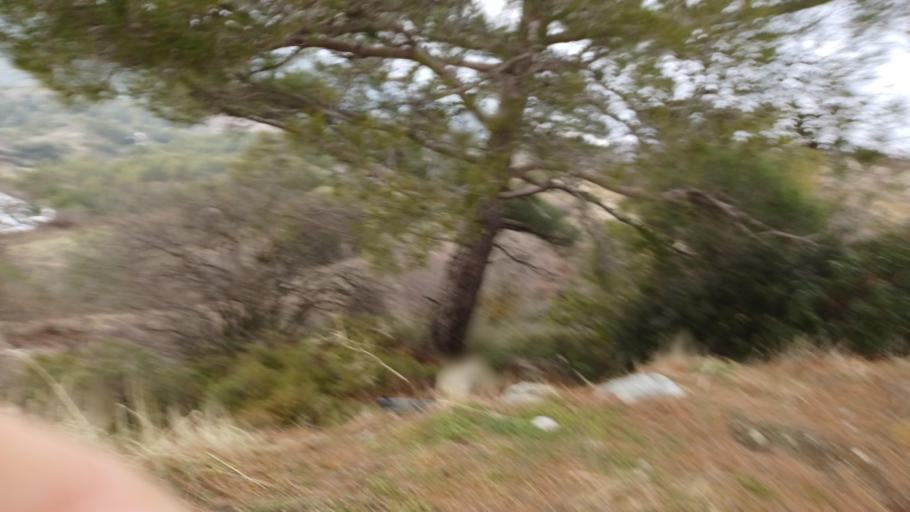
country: CY
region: Limassol
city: Kyperounta
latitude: 34.9255
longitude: 32.9665
